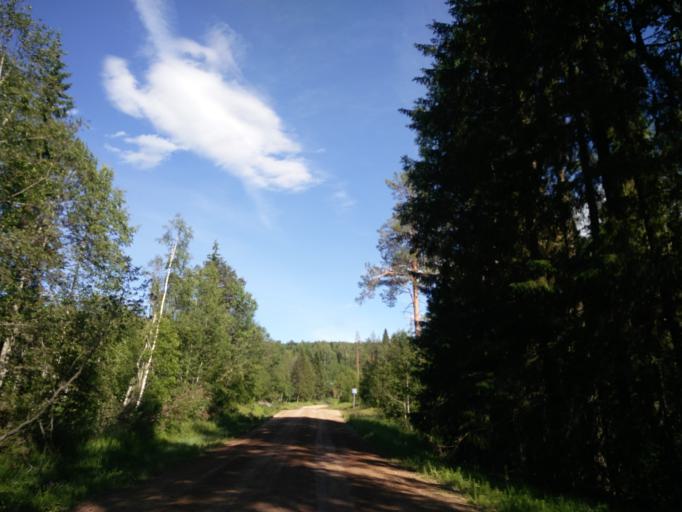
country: SE
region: Vaesternorrland
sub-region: Ange Kommun
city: Fransta
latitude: 62.2039
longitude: 16.3560
